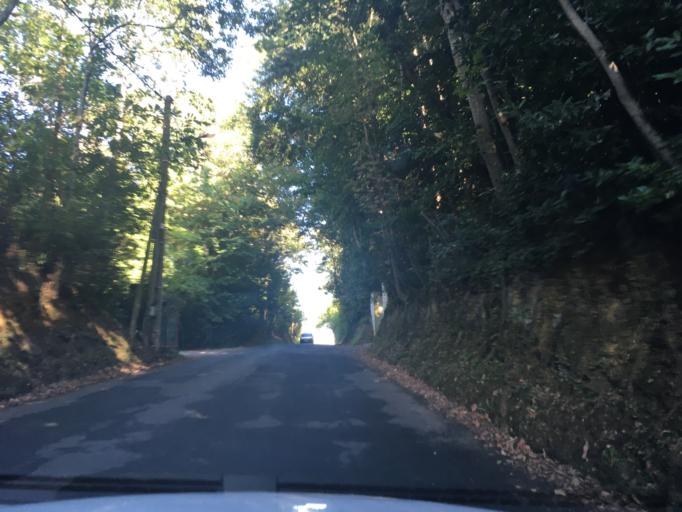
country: FR
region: Aquitaine
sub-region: Departement des Pyrenees-Atlantiques
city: Biarritz
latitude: 43.4678
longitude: -1.5455
